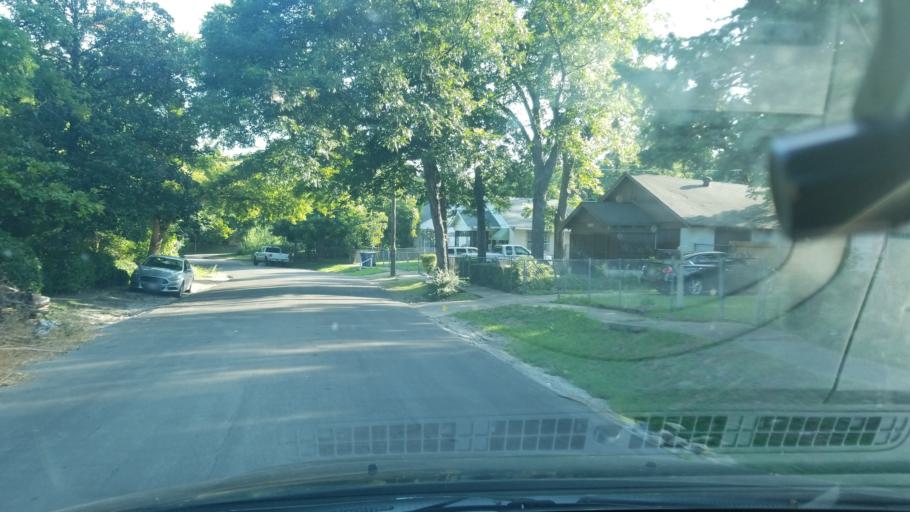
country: US
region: Texas
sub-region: Dallas County
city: Dallas
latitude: 32.7230
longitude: -96.8180
